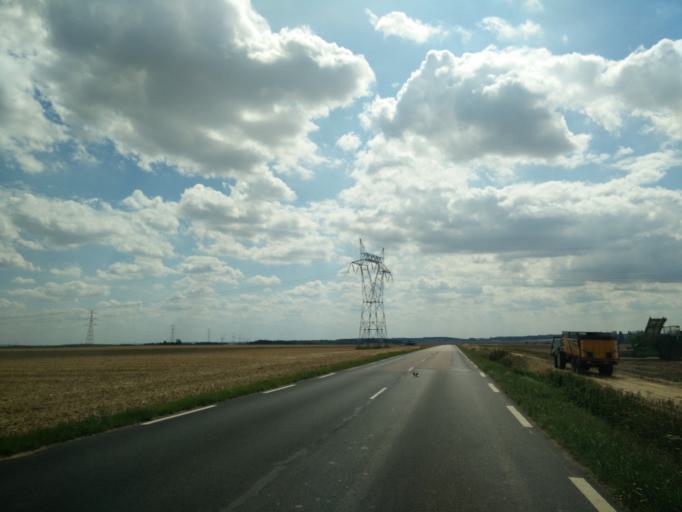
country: FR
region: Ile-de-France
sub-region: Departement des Yvelines
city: Guerville
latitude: 48.9278
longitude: 1.7280
